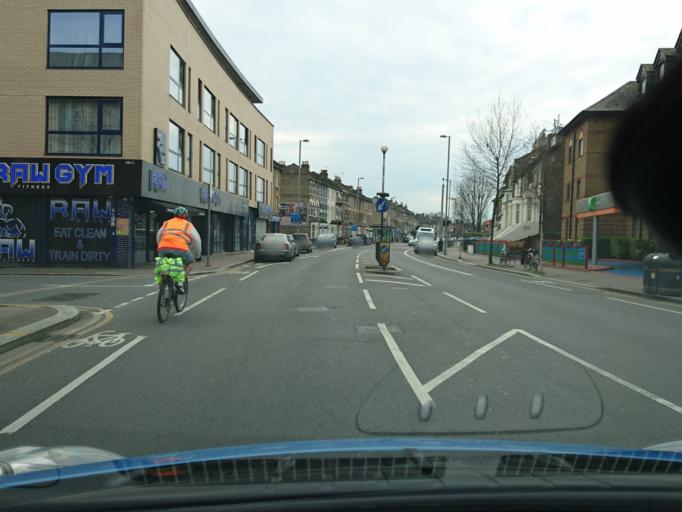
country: GB
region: England
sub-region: Greater London
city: Walthamstow
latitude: 51.5737
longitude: -0.0151
